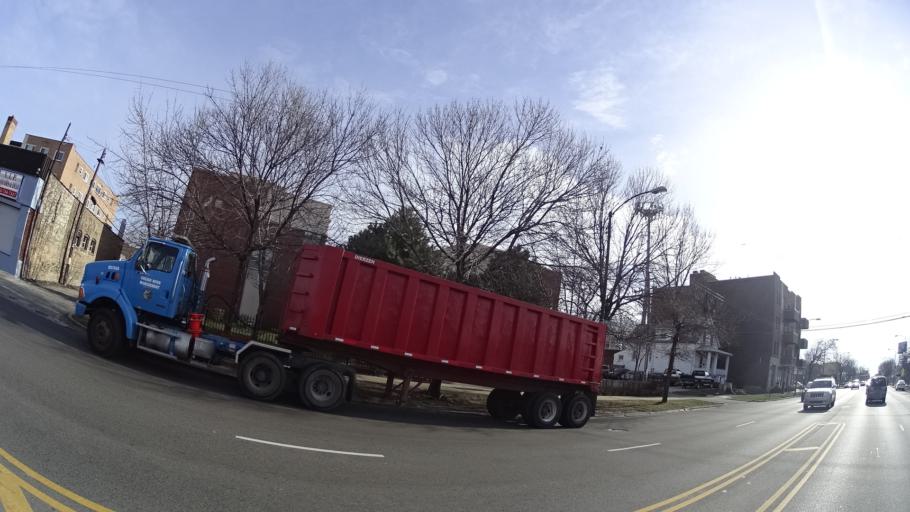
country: US
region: Illinois
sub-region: Cook County
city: Evanston
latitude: 42.0081
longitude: -87.6902
